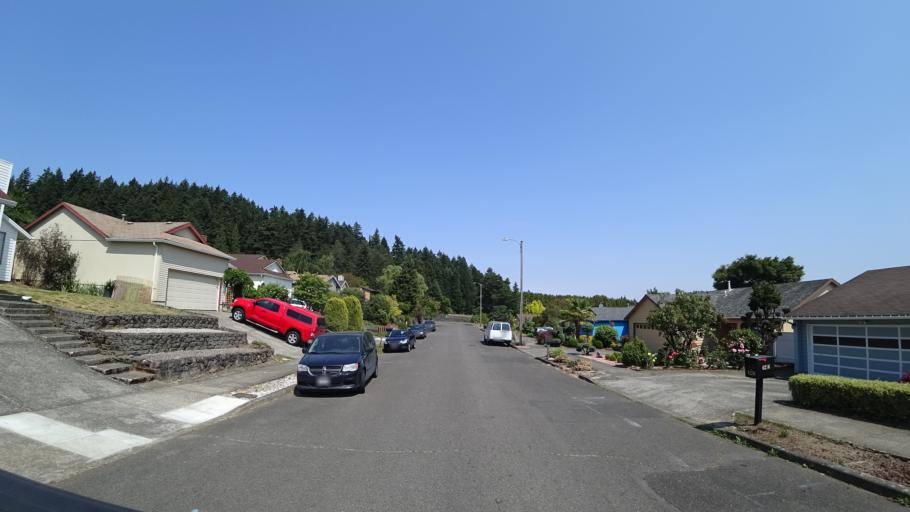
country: US
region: Oregon
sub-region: Multnomah County
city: Lents
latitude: 45.5074
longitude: -122.5989
